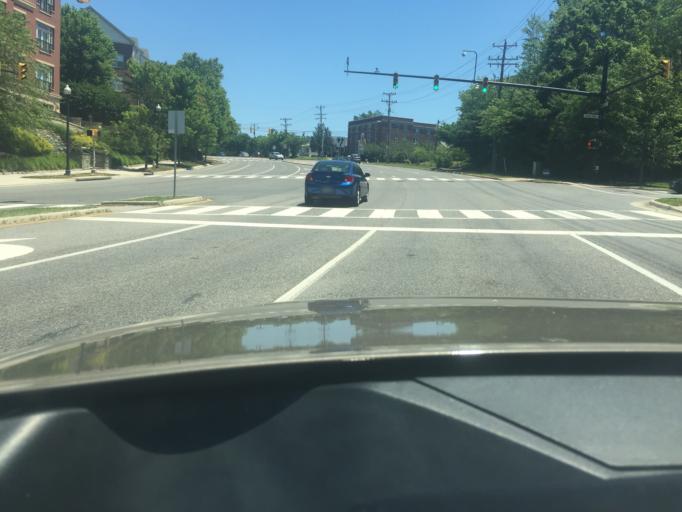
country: US
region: Virginia
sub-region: Arlington County
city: Arlington
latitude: 38.8950
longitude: -77.0946
